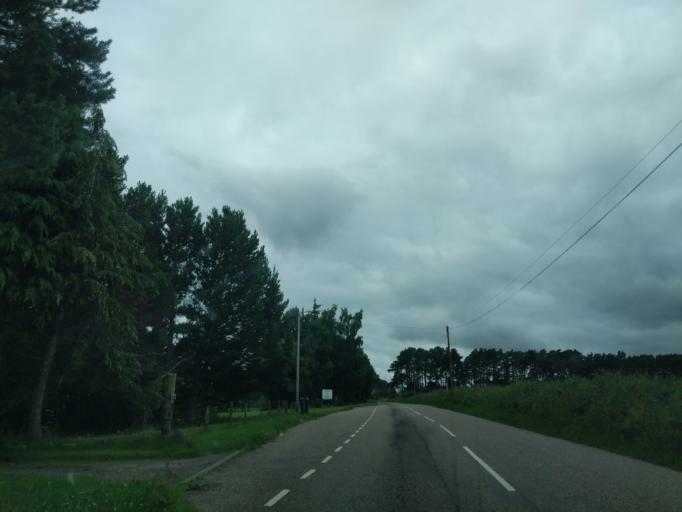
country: GB
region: Scotland
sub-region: Moray
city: Rothes
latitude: 57.4890
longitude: -3.2425
